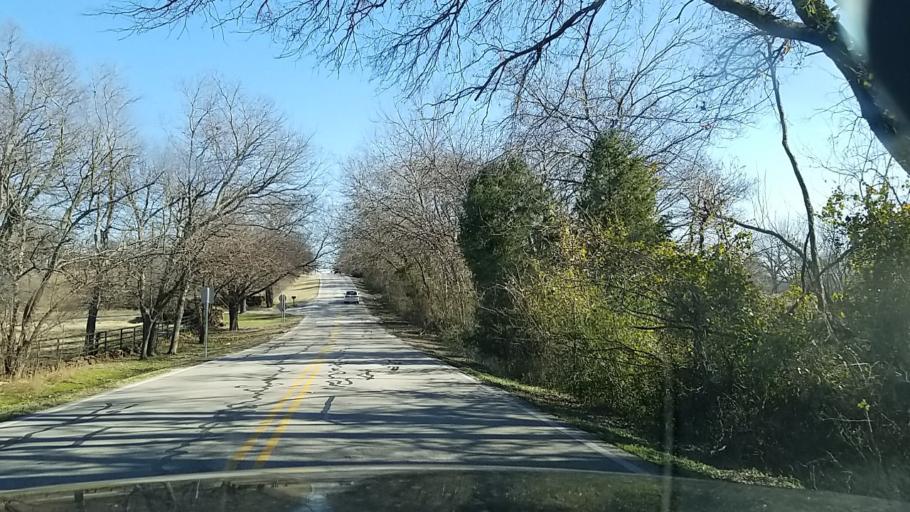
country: US
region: Texas
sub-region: Denton County
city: Argyle
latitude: 33.1471
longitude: -97.1313
